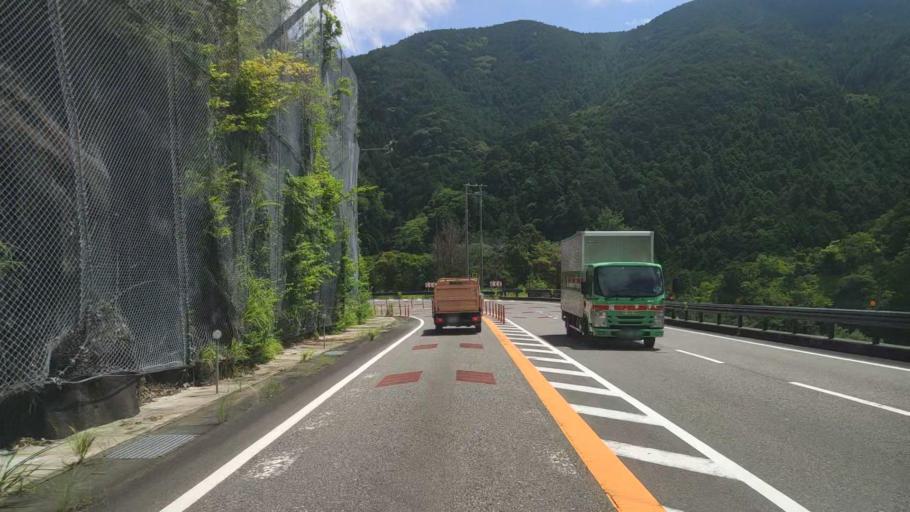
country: JP
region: Mie
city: Owase
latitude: 33.9190
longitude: 136.1024
